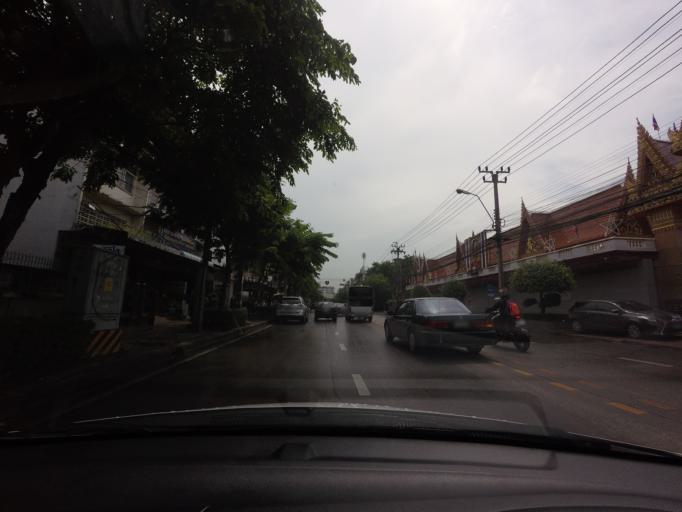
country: TH
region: Bangkok
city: Phra Khanong
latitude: 13.7092
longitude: 100.6202
